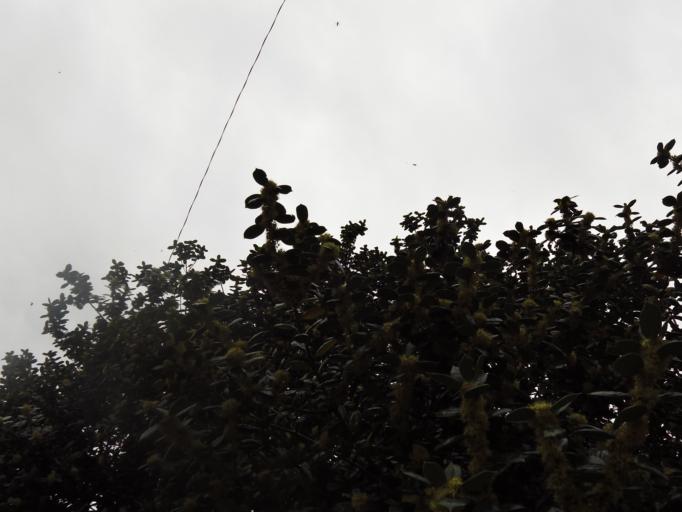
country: US
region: Tennessee
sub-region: Knox County
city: Knoxville
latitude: 35.9564
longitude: -83.9412
